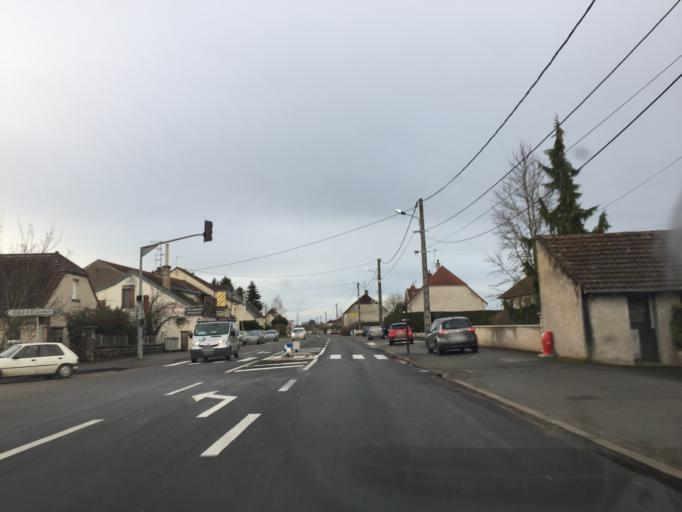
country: FR
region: Franche-Comte
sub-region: Departement du Jura
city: Dole
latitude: 47.0700
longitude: 5.4965
